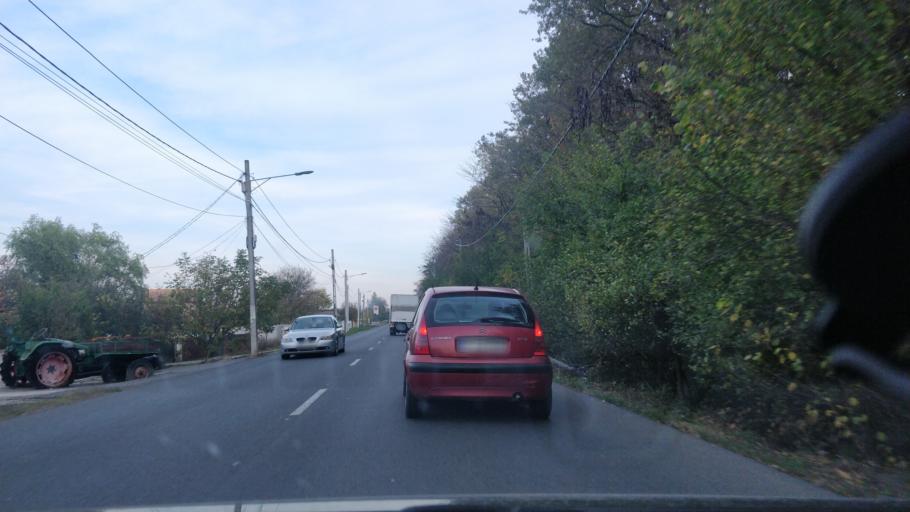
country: RO
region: Ilfov
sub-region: Comuna Ciorogarla
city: Ciorogarla
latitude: 44.4458
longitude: 25.8596
